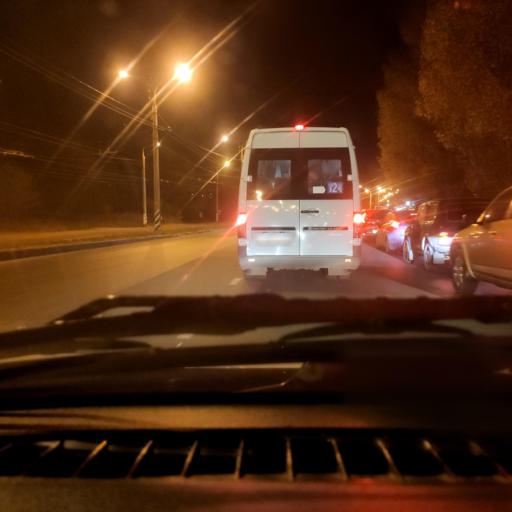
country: RU
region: Samara
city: Zhigulevsk
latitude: 53.4878
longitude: 49.5050
